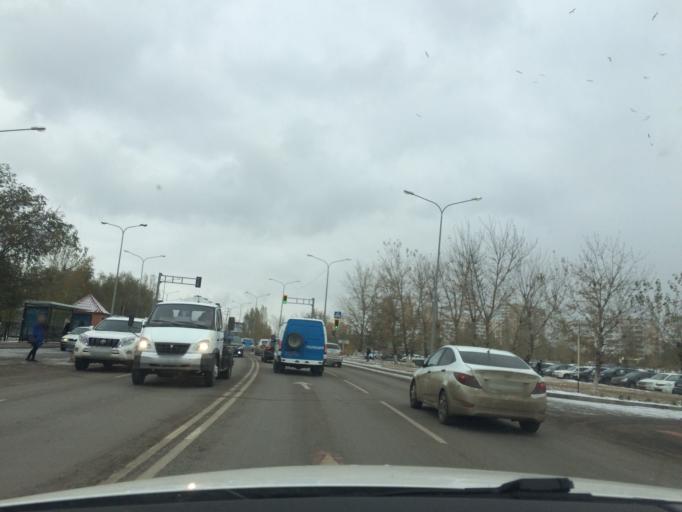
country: KZ
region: Astana Qalasy
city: Astana
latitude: 51.1593
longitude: 71.4655
